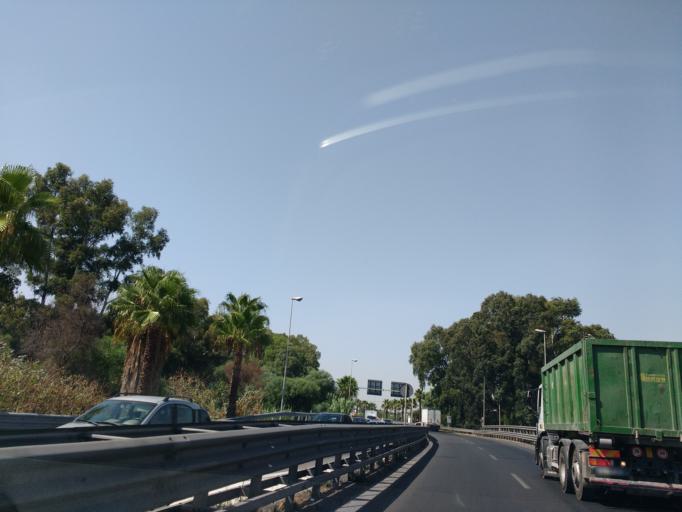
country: IT
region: Sicily
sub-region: Catania
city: Catania
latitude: 37.4876
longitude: 15.0819
